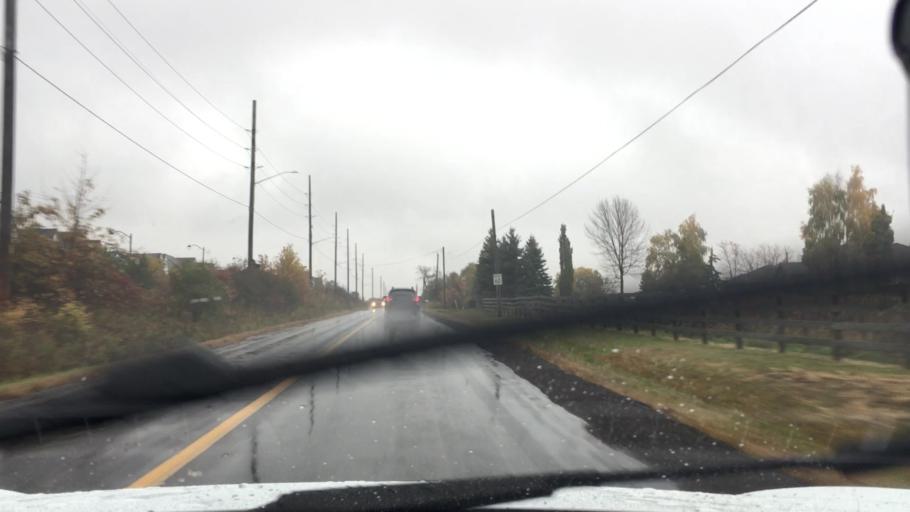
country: CA
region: Ontario
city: Oshawa
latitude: 43.9515
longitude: -78.8331
